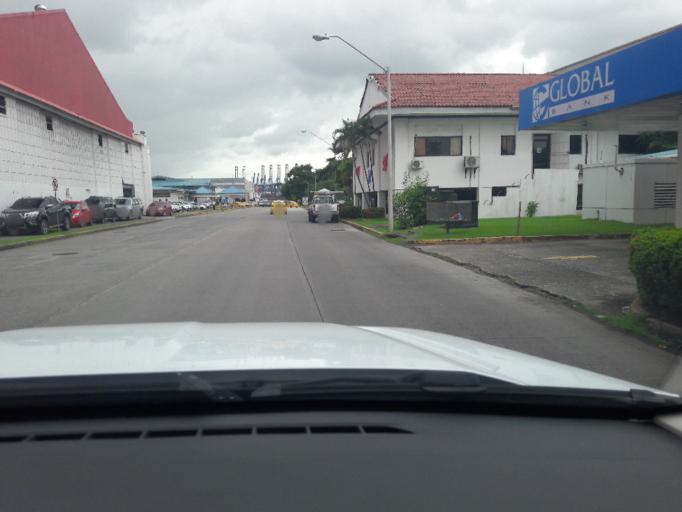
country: PA
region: Panama
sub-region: Distrito de Panama
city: Ancon
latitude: 8.9724
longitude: -79.5594
